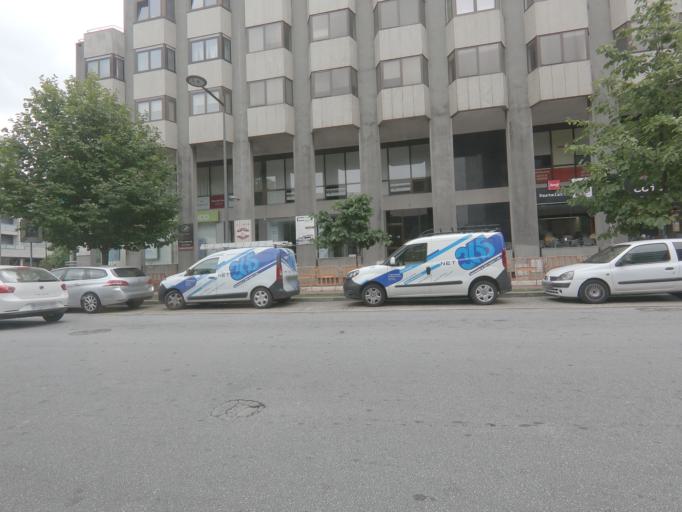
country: PT
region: Viana do Castelo
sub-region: Valenca
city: Valenza
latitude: 42.0247
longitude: -8.6419
